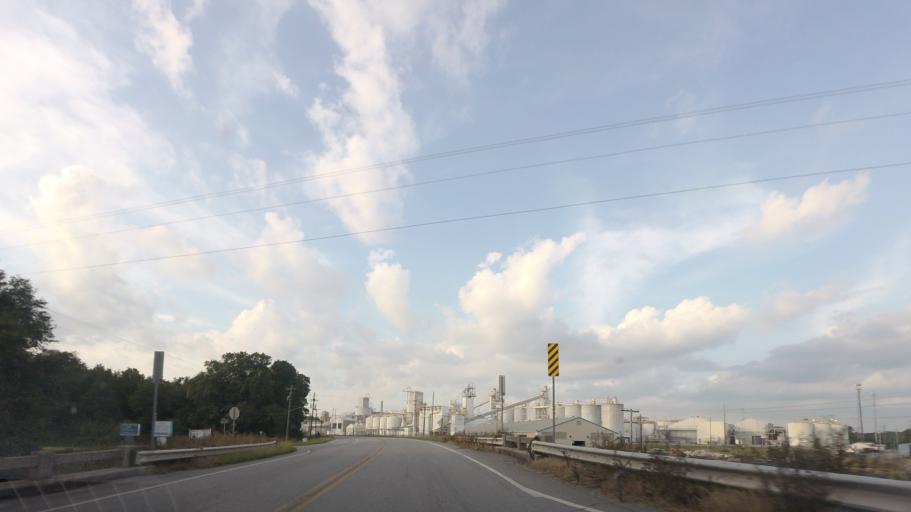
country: US
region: Georgia
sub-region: Wilkinson County
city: Gordon
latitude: 32.8778
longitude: -83.3398
